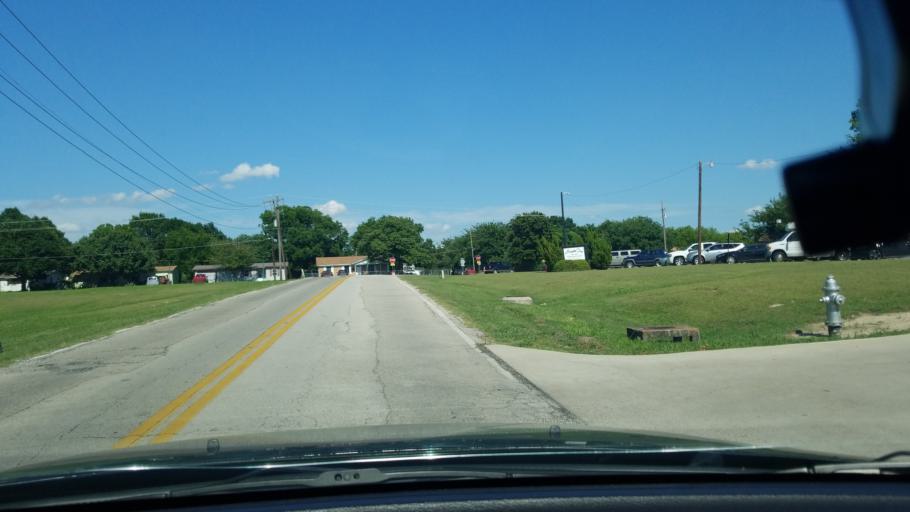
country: US
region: Texas
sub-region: Dallas County
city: Mesquite
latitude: 32.7548
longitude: -96.5934
